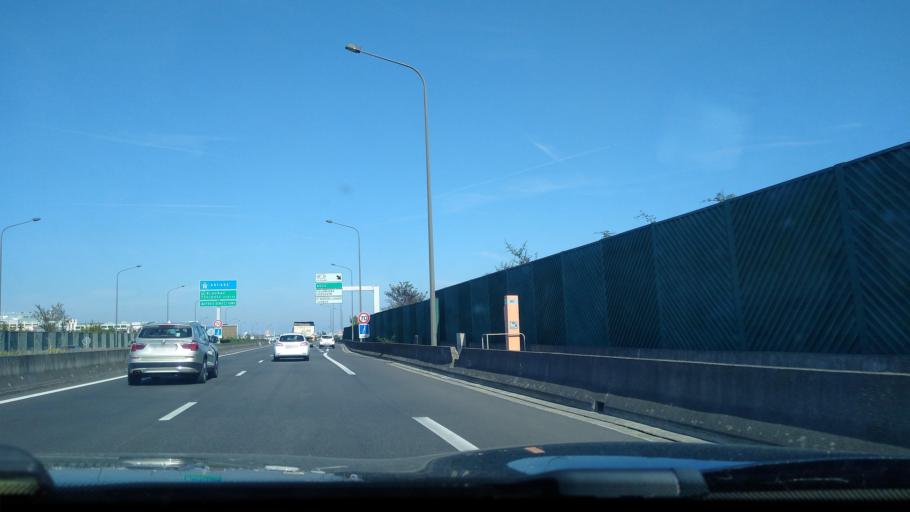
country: FR
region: Midi-Pyrenees
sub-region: Departement de la Haute-Garonne
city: Colomiers
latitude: 43.6050
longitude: 1.3678
